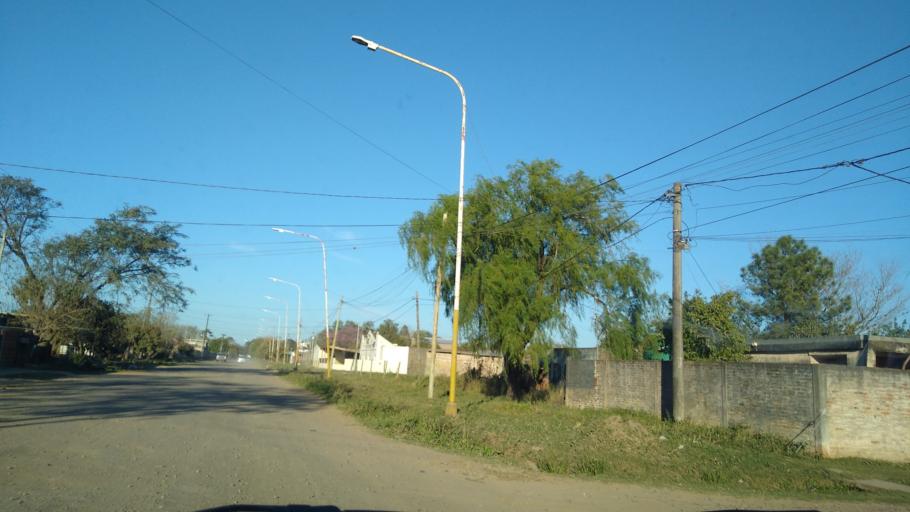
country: AR
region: Chaco
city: Barranqueras
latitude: -27.4782
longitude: -58.9453
